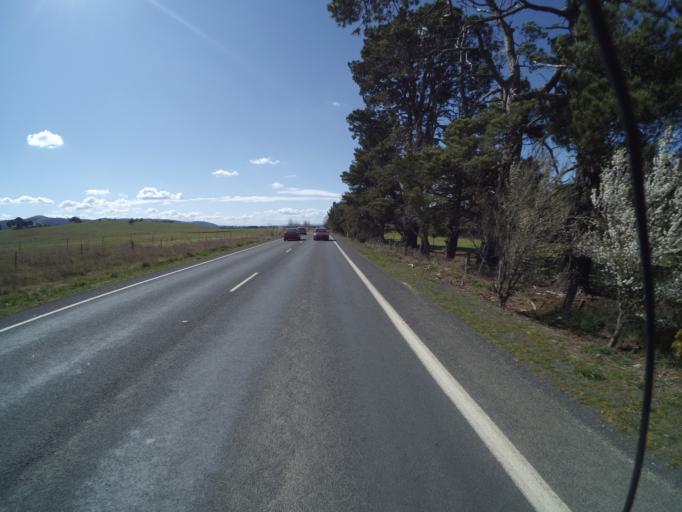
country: AU
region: New South Wales
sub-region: Palerang
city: Bungendore
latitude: -35.2889
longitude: 149.4207
